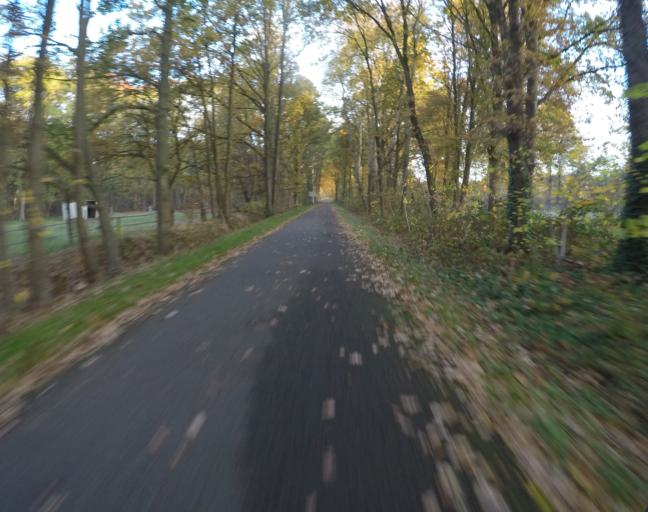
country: BE
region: Flanders
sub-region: Provincie Antwerpen
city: Hulshout
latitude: 51.0753
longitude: 4.8252
